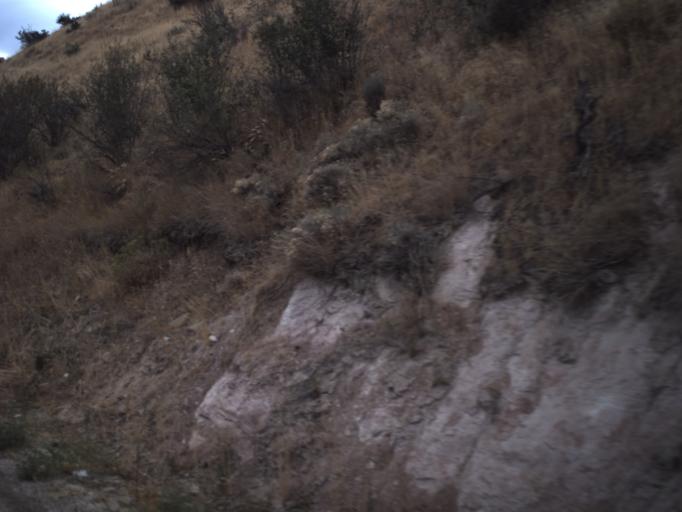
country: US
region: Utah
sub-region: Morgan County
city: Morgan
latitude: 40.9955
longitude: -111.6821
